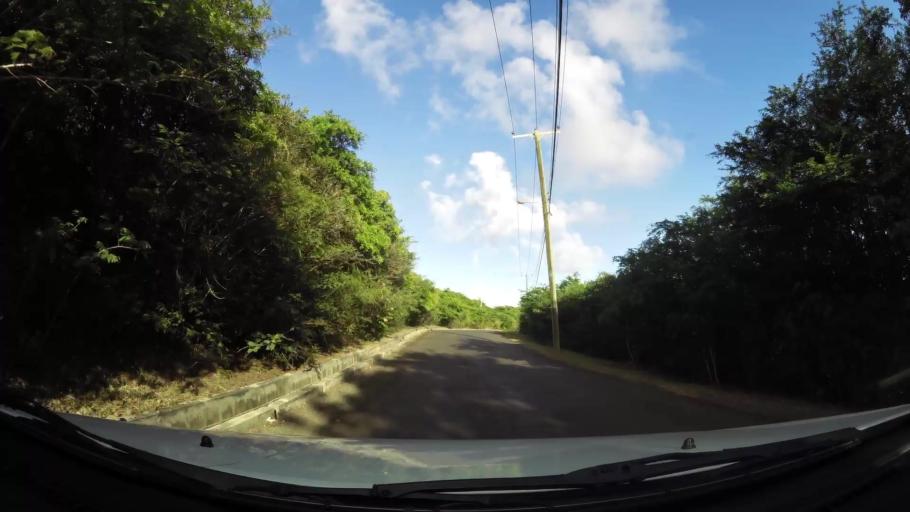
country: LC
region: Gros-Islet
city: Gros Islet
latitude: 14.0968
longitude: -60.9359
